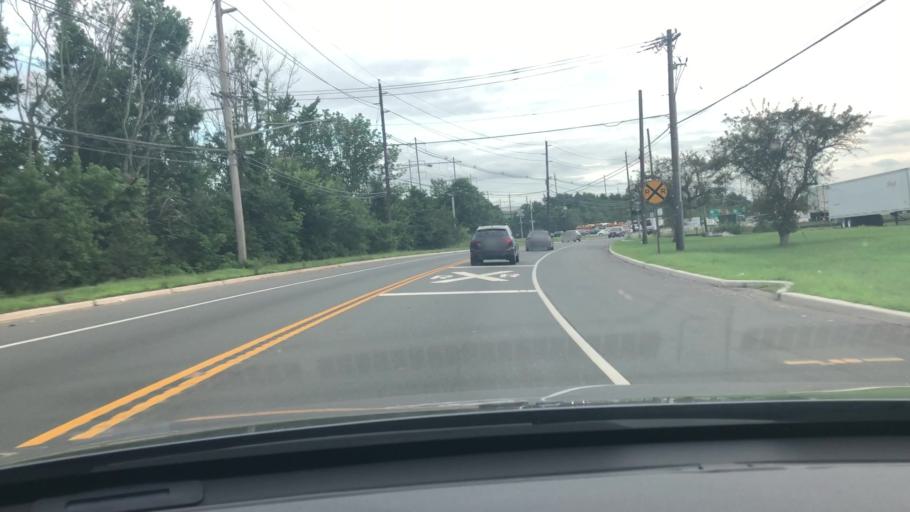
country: US
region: New Jersey
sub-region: Somerset County
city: Somerset
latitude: 40.4579
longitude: -74.4851
